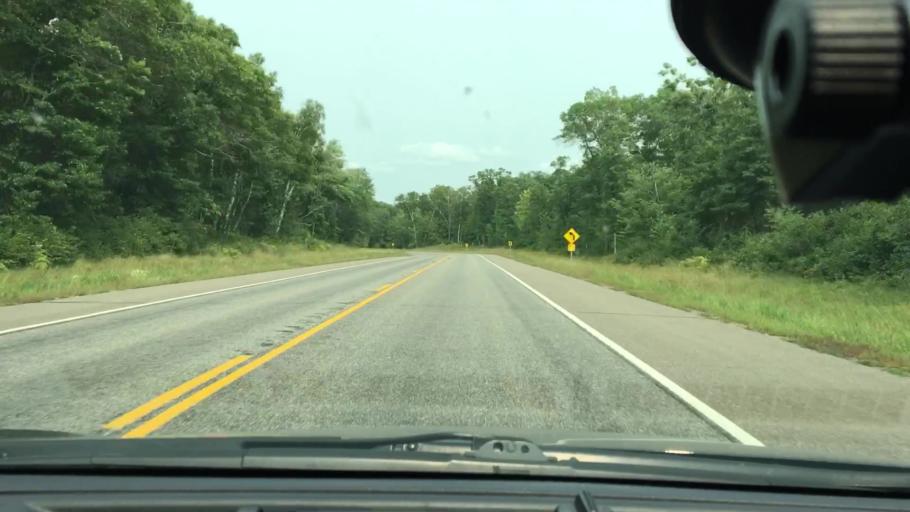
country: US
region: Minnesota
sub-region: Crow Wing County
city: Cross Lake
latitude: 46.6956
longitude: -94.0690
